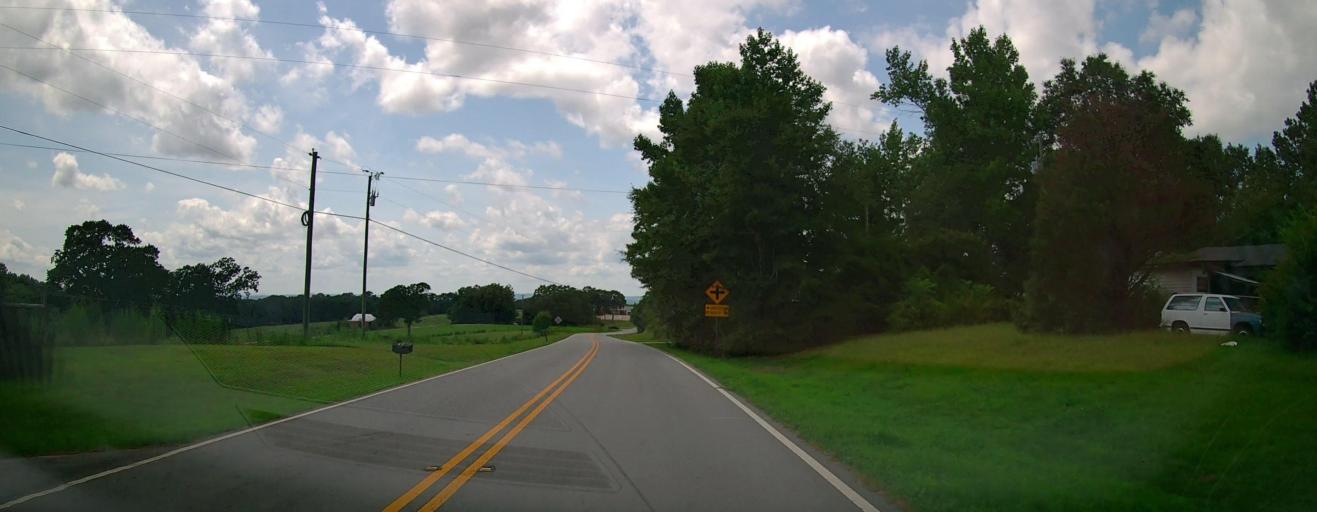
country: US
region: Georgia
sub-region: Carroll County
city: Bowdon
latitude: 33.4401
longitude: -85.2774
